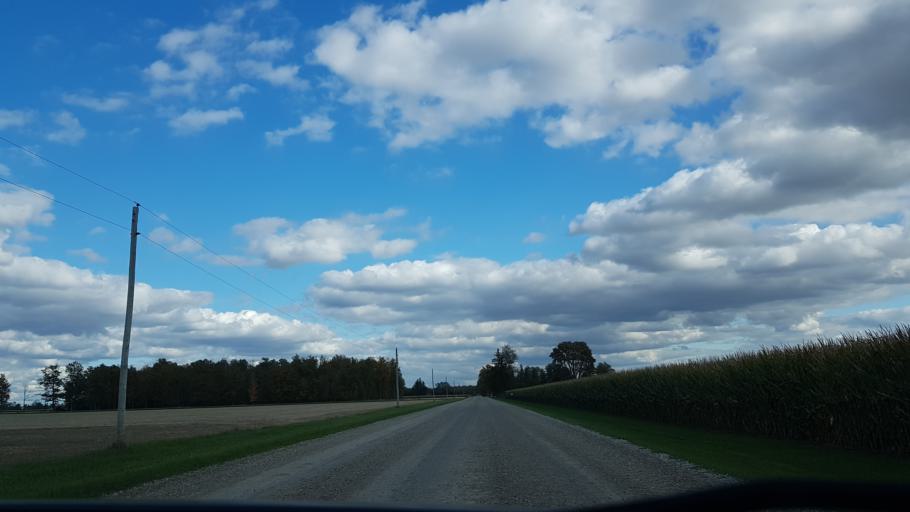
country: CA
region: Ontario
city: South Huron
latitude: 43.1092
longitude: -81.6270
